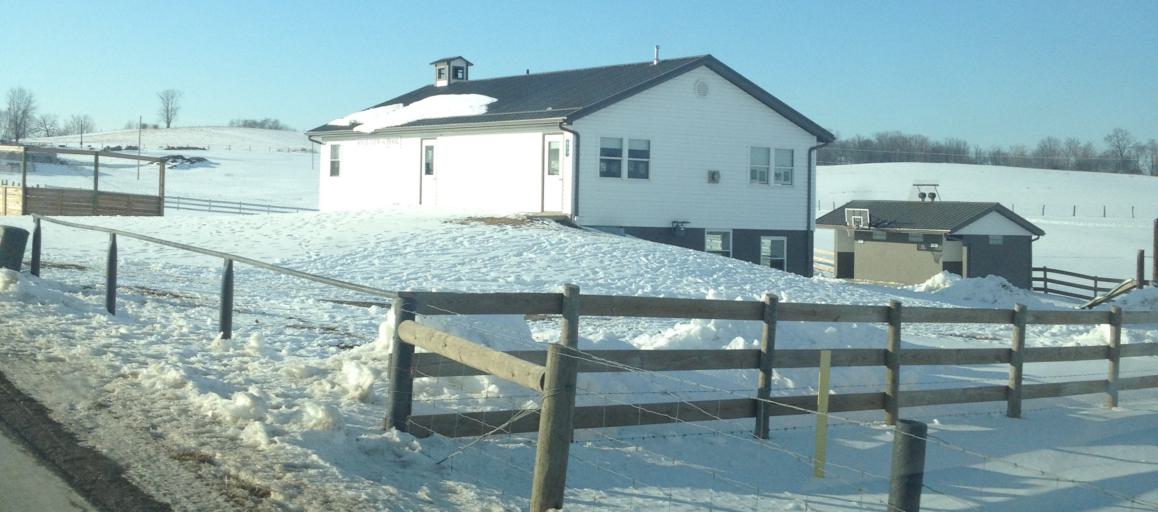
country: US
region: Ohio
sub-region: Tuscarawas County
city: Sugarcreek
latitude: 40.4575
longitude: -81.7794
